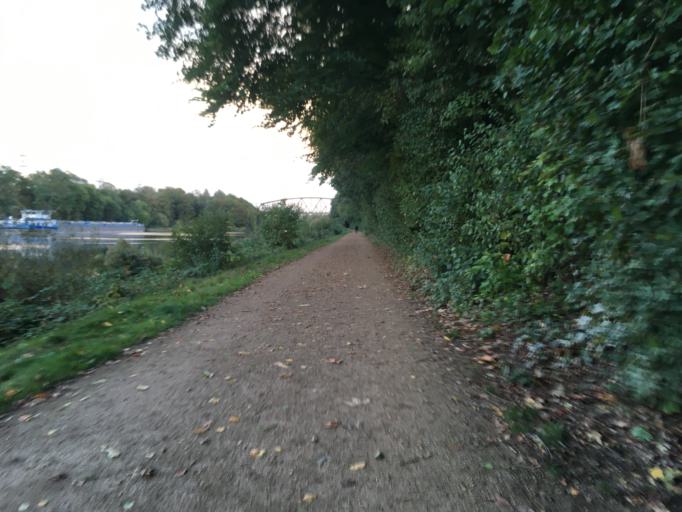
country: DE
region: North Rhine-Westphalia
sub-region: Regierungsbezirk Munster
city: Bottrop
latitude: 51.4945
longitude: 6.9150
